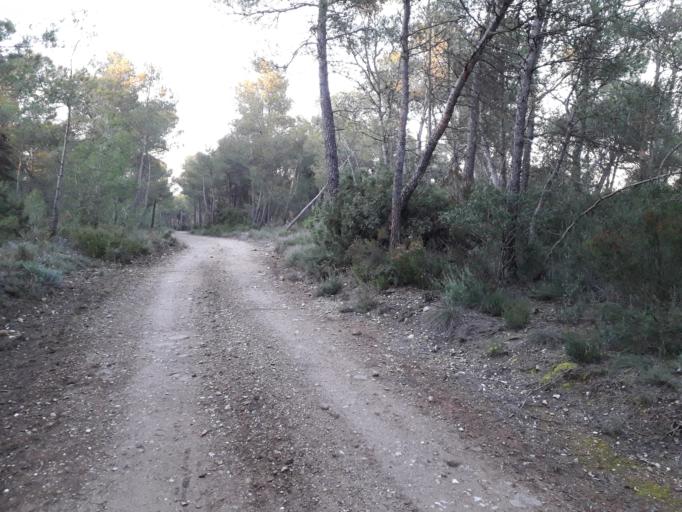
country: ES
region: Catalonia
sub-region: Provincia de Barcelona
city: Sant Marti de Tous
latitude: 41.5567
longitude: 1.5477
